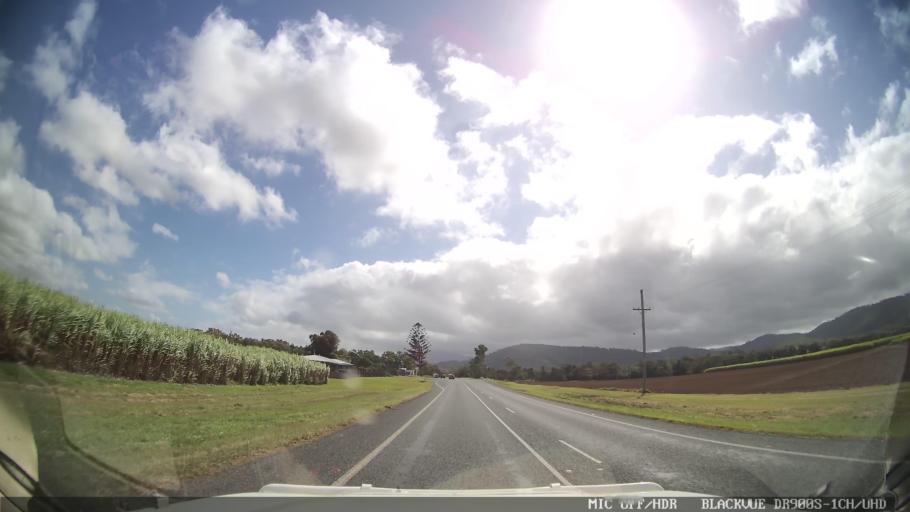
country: AU
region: Queensland
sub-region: Whitsunday
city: Proserpine
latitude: -20.3536
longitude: 148.5562
